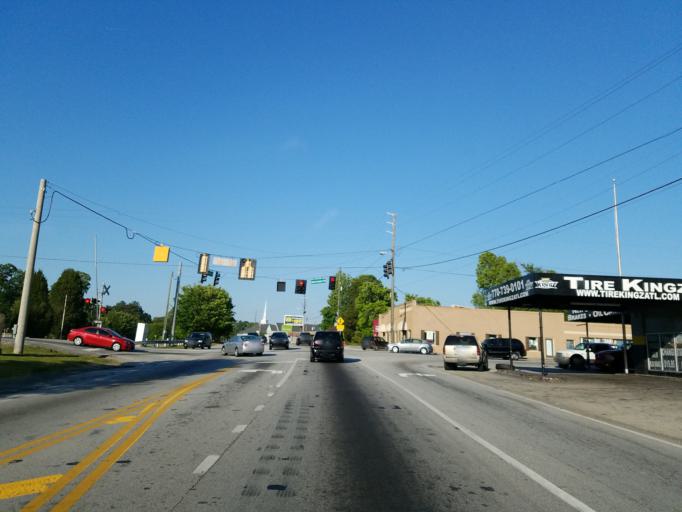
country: US
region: Georgia
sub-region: Douglas County
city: Lithia Springs
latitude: 33.7939
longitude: -84.6614
